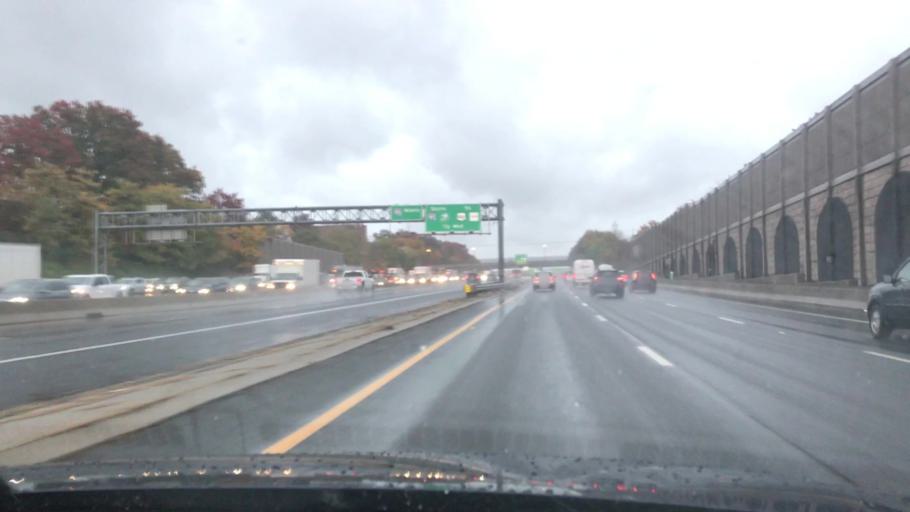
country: US
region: New Jersey
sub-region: Bergen County
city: Bogota
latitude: 40.8666
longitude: -74.0272
